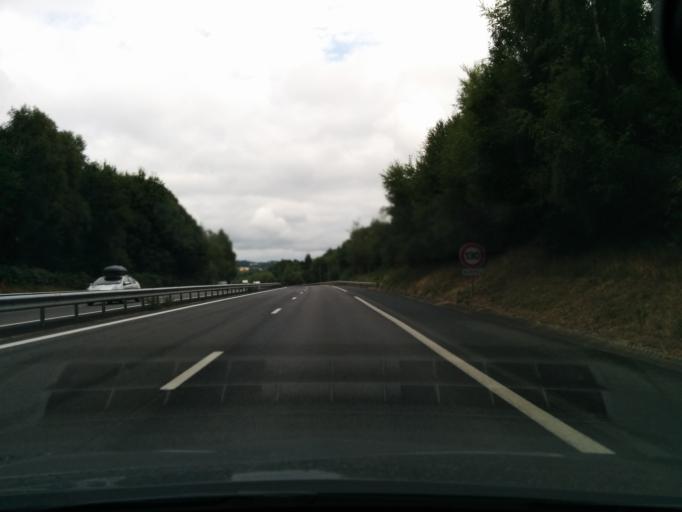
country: FR
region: Limousin
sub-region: Departement de la Correze
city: Uzerche
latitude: 45.3689
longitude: 1.5726
